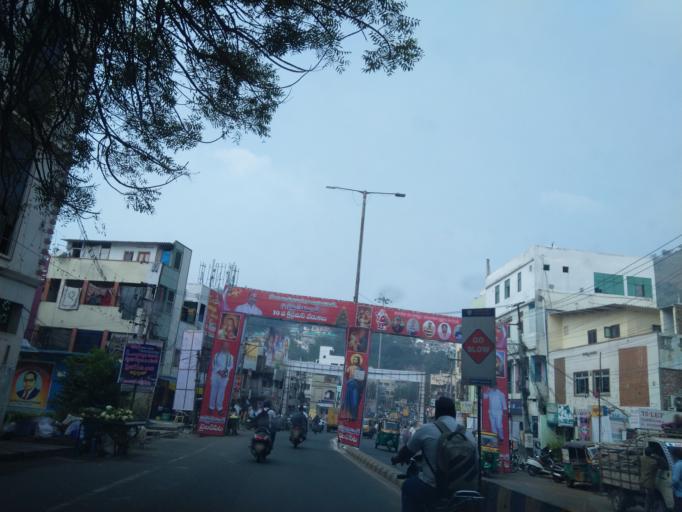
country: IN
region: Andhra Pradesh
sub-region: Krishna
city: Vijayawada
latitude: 16.5304
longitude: 80.6132
